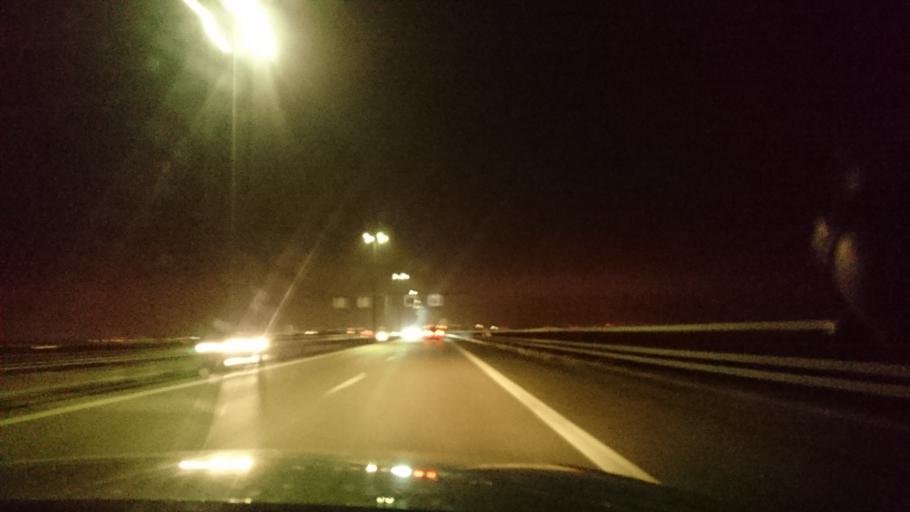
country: SE
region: Skane
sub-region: Malmo
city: Bunkeflostrand
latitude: 55.5677
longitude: 12.8668
